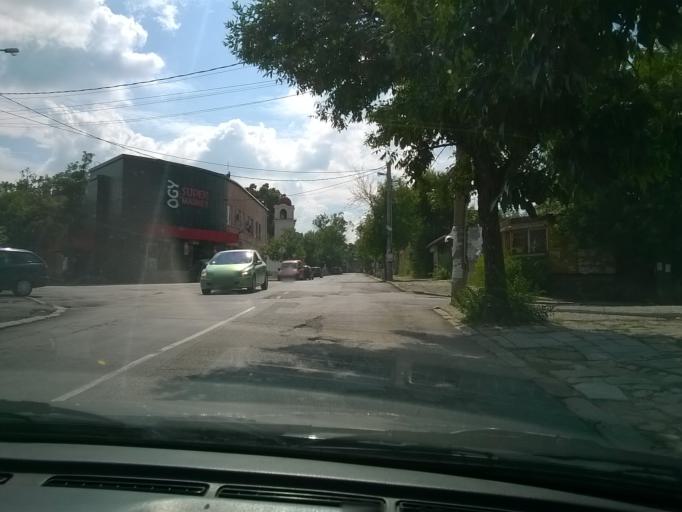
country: BG
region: Sofiya
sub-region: Obshtina Bozhurishte
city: Bozhurishte
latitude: 42.6776
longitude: 23.2398
